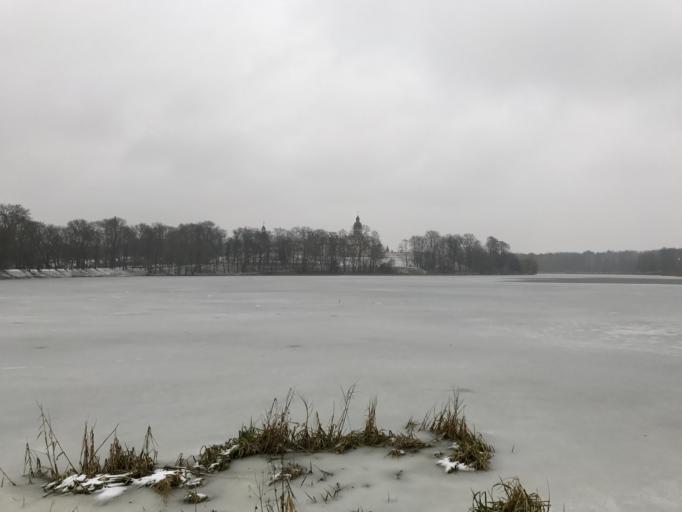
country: BY
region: Minsk
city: Nyasvizh
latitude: 53.2202
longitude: 26.6861
